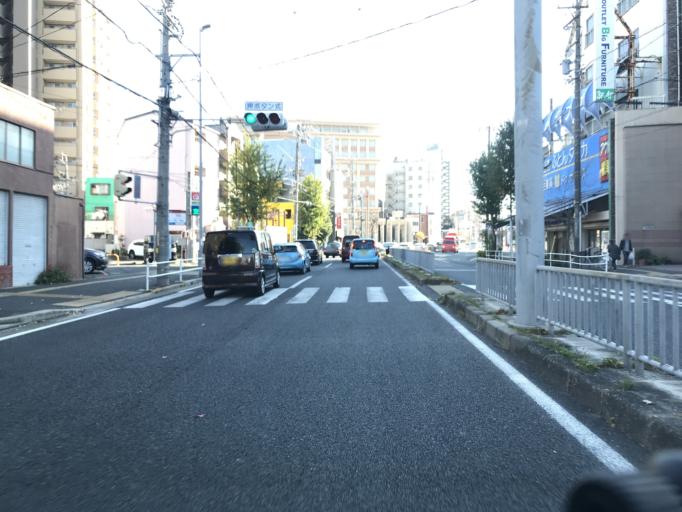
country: JP
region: Aichi
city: Nagoya-shi
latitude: 35.1915
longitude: 136.9302
